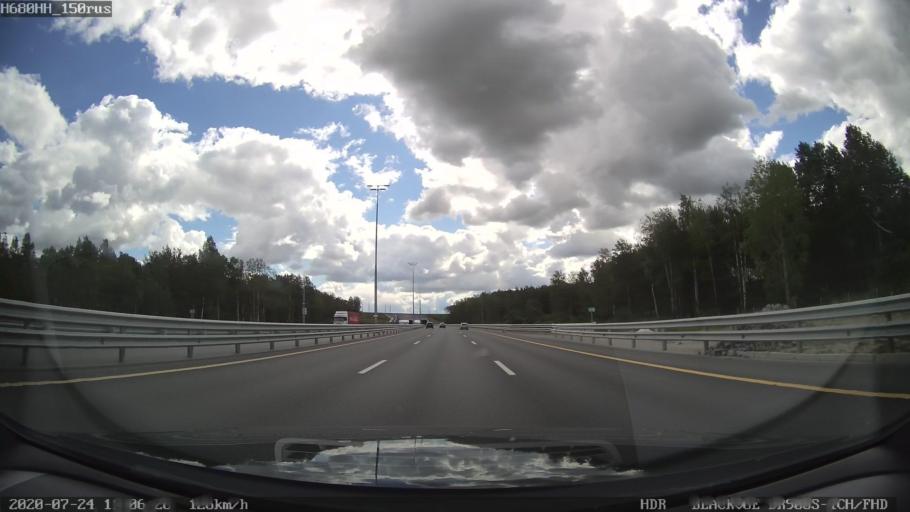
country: RU
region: St.-Petersburg
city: Shushary
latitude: 59.7629
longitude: 30.3769
